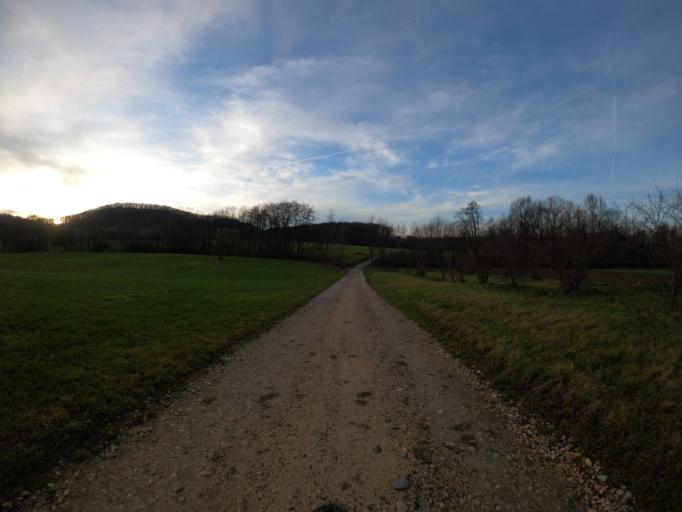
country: DE
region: Baden-Wuerttemberg
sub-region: Regierungsbezirk Stuttgart
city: Zell unter Aichelberg
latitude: 48.6380
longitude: 9.5886
